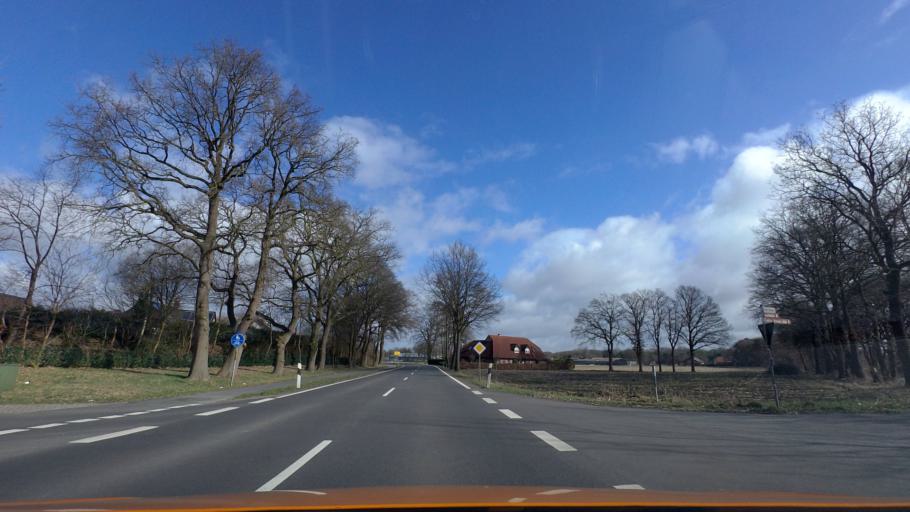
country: DE
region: Lower Saxony
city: Bosel
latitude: 53.0016
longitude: 7.9622
